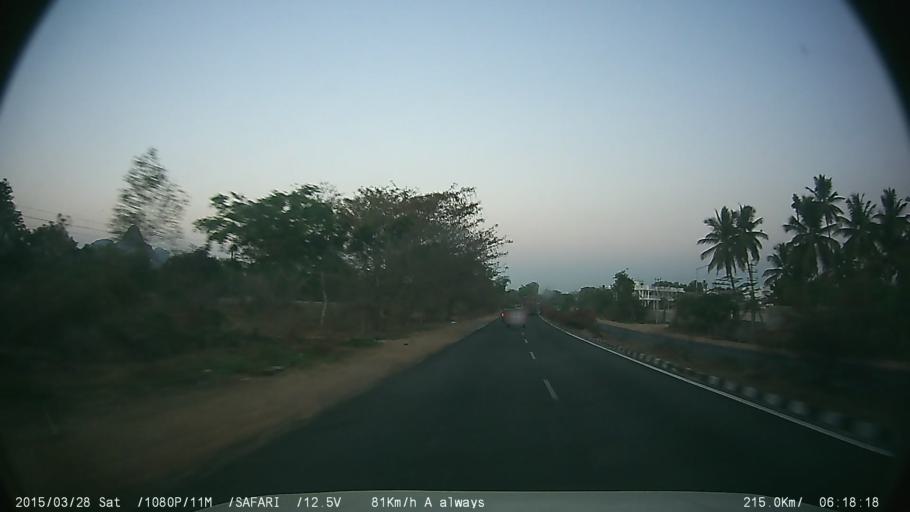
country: IN
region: Karnataka
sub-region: Ramanagara
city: Ramanagaram
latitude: 12.7396
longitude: 77.3061
